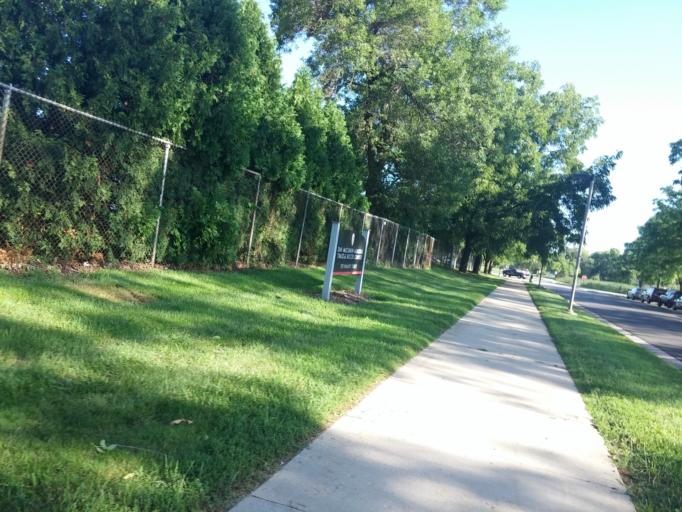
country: US
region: Wisconsin
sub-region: Dane County
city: Shorewood Hills
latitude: 43.0777
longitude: -89.4252
